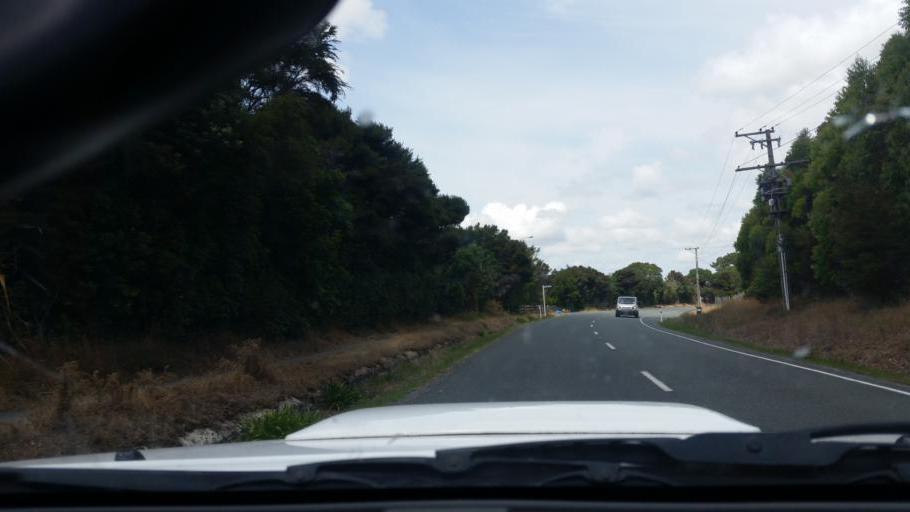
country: NZ
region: Auckland
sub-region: Auckland
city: Wellsford
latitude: -36.1146
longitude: 174.5751
